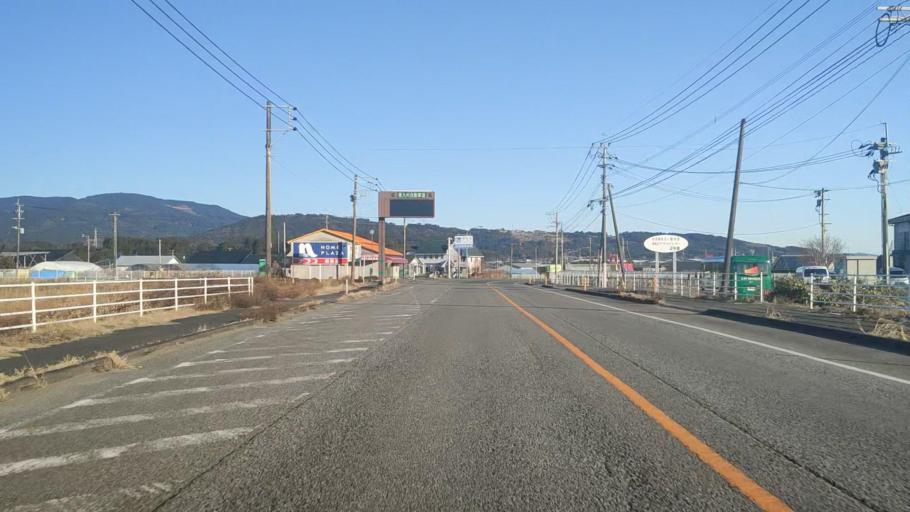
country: JP
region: Miyazaki
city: Takanabe
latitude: 32.2483
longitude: 131.5517
